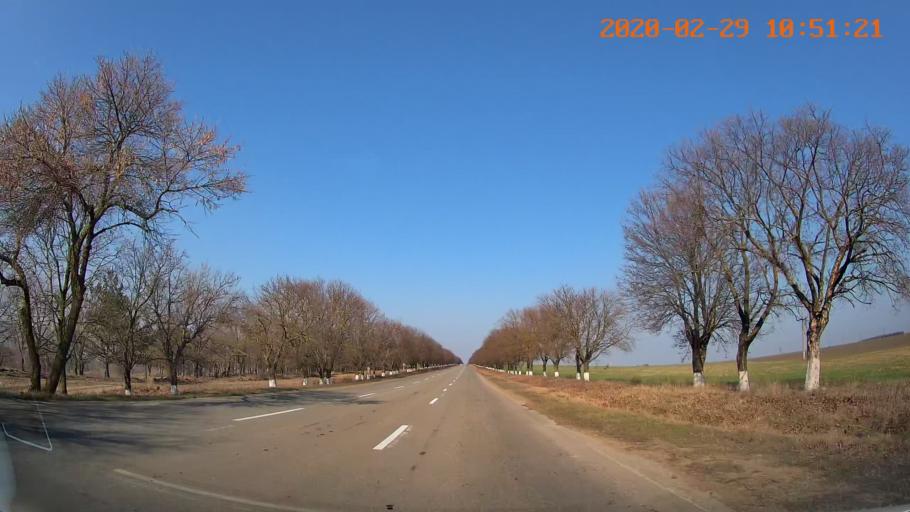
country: MD
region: Telenesti
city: Grigoriopol
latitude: 47.0923
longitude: 29.3654
